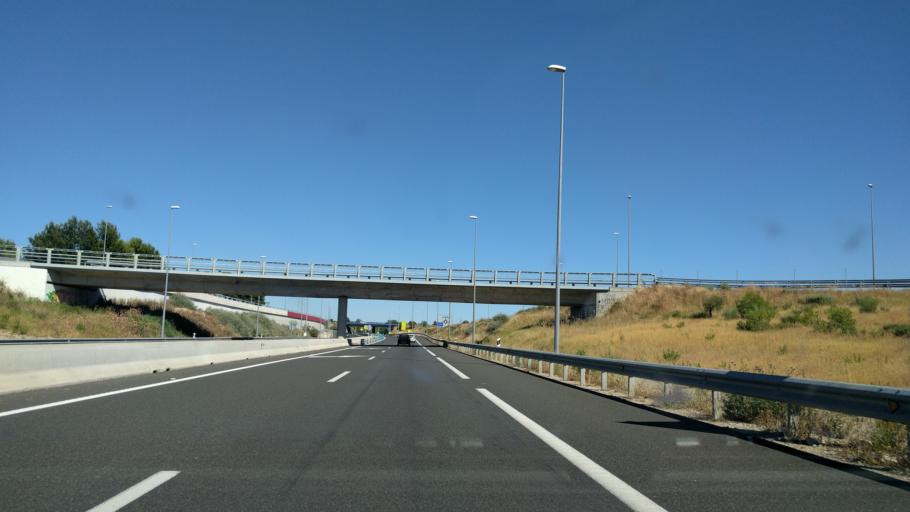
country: ES
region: Catalonia
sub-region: Provincia de Lleida
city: Alpicat
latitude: 41.6483
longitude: 0.5605
